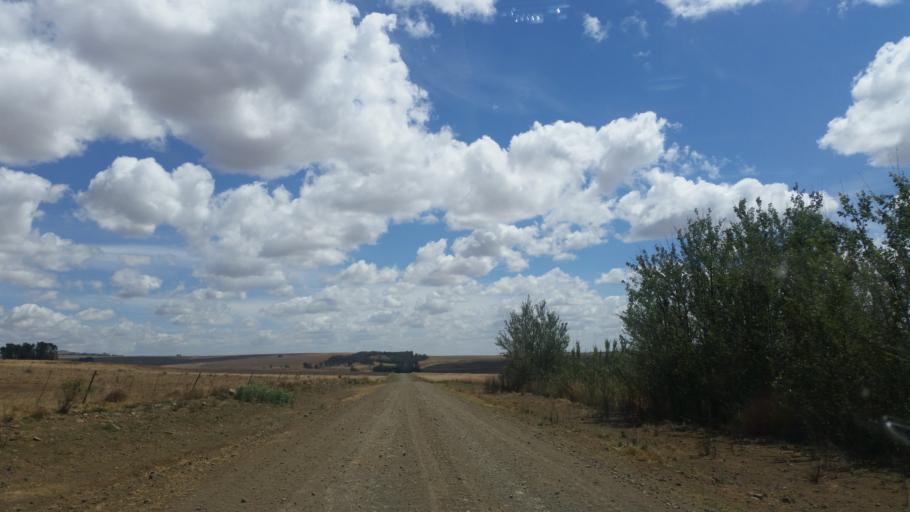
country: ZA
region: Orange Free State
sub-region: Thabo Mofutsanyana District Municipality
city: Bethlehem
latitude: -28.1913
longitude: 28.6036
